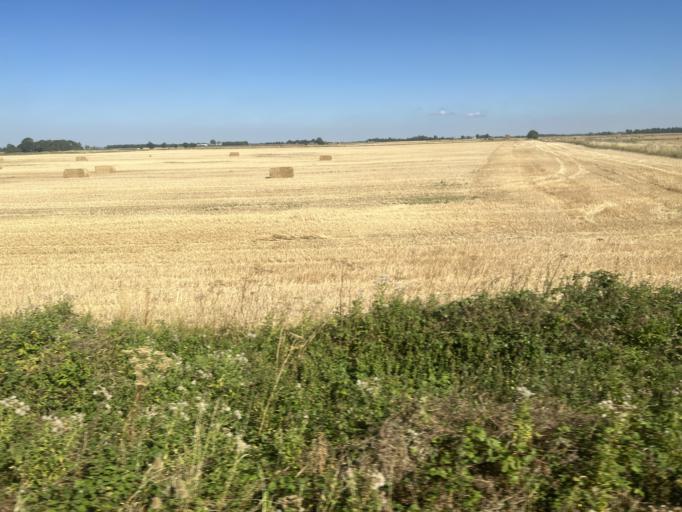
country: GB
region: England
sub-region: Lincolnshire
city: Donington
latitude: 52.9665
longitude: -0.2254
